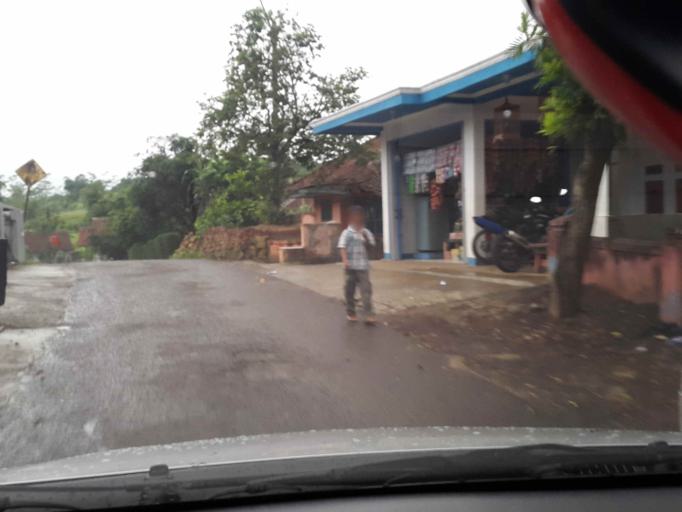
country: ID
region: West Java
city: Sukabumi
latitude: -6.9201
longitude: 106.8606
